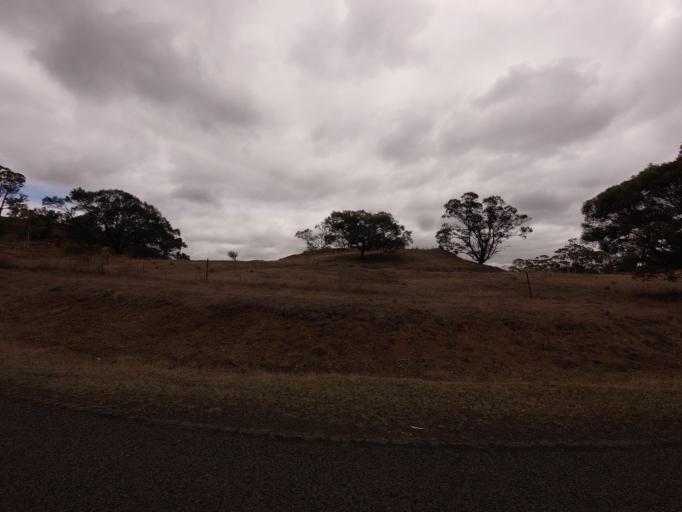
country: AU
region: Tasmania
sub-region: Clarence
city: Cambridge
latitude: -42.7914
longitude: 147.4023
